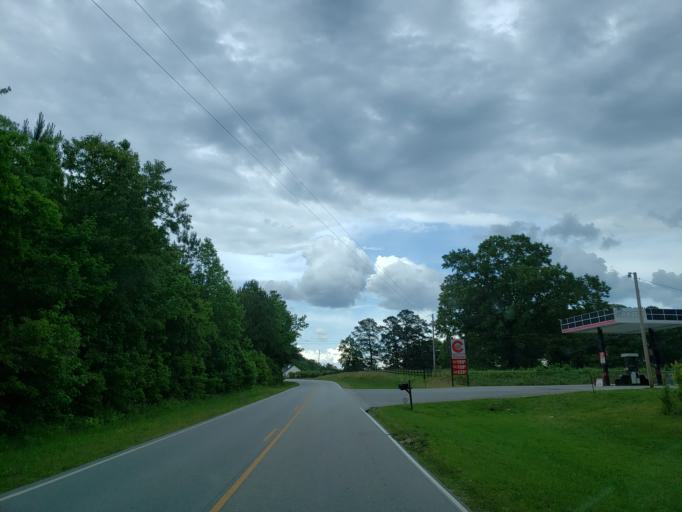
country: US
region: Georgia
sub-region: Polk County
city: Rockmart
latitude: 33.9029
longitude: -85.0708
